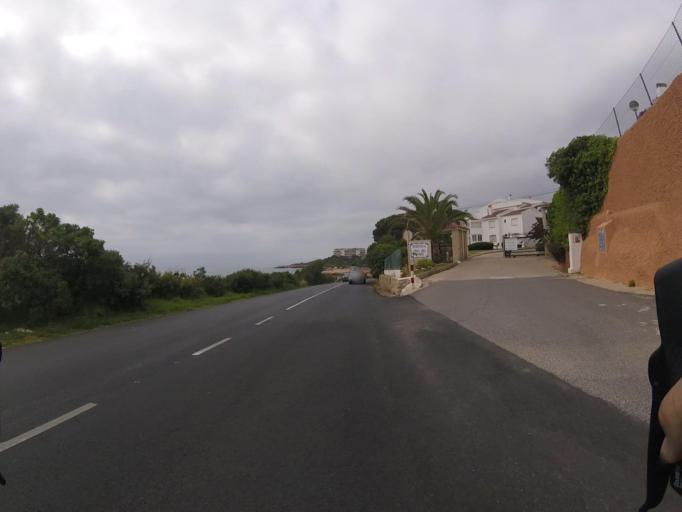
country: ES
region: Valencia
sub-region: Provincia de Castello
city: Peniscola
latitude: 40.3487
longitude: 0.3907
